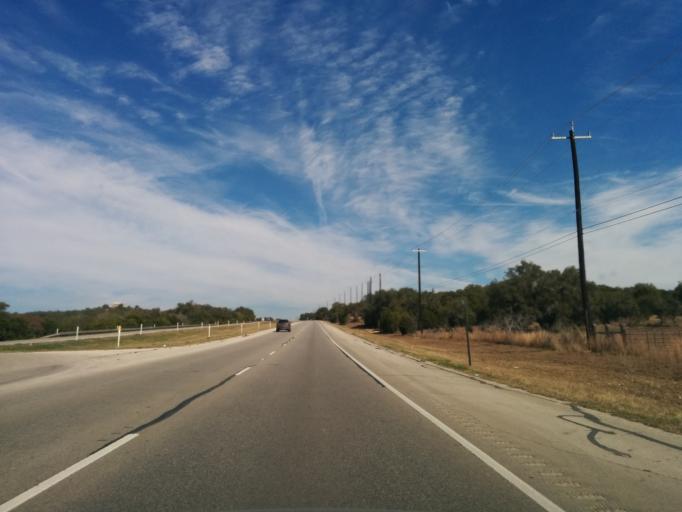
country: US
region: Texas
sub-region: Comal County
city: Bulverde
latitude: 29.7544
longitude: -98.4308
